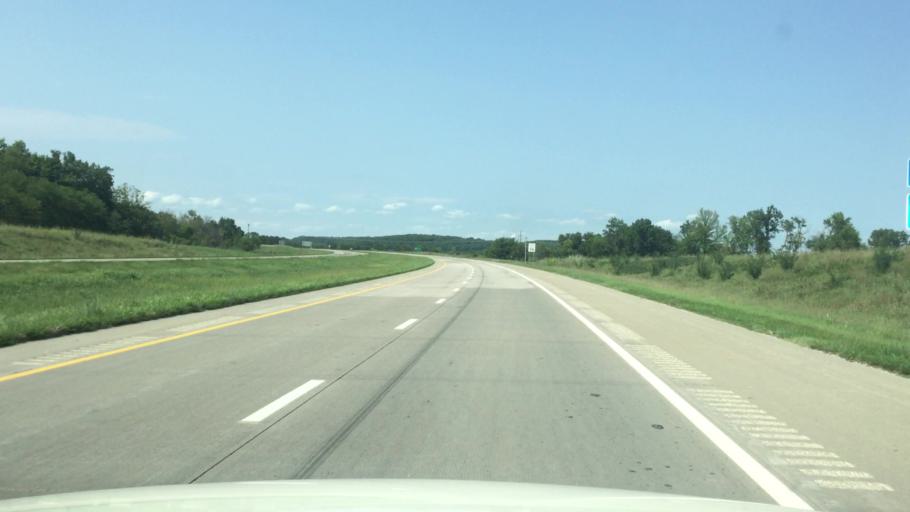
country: US
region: Kansas
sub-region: Linn County
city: Pleasanton
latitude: 38.2694
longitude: -94.6685
